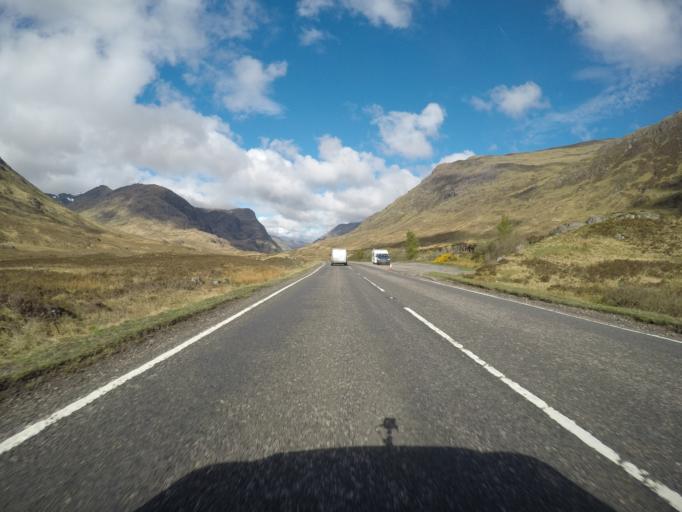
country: GB
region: Scotland
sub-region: Highland
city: Fort William
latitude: 56.6643
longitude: -4.9438
